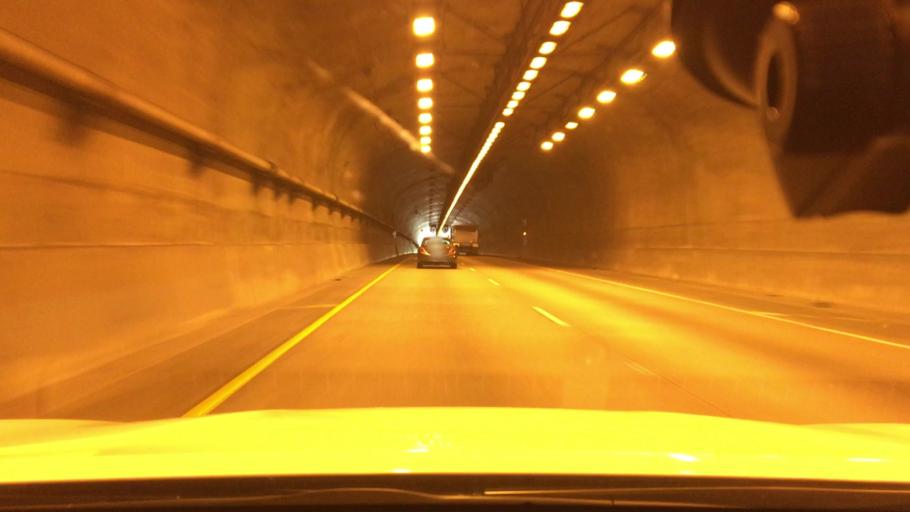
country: US
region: Arkansas
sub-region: Washington County
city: West Fork
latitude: 35.7671
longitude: -94.1897
